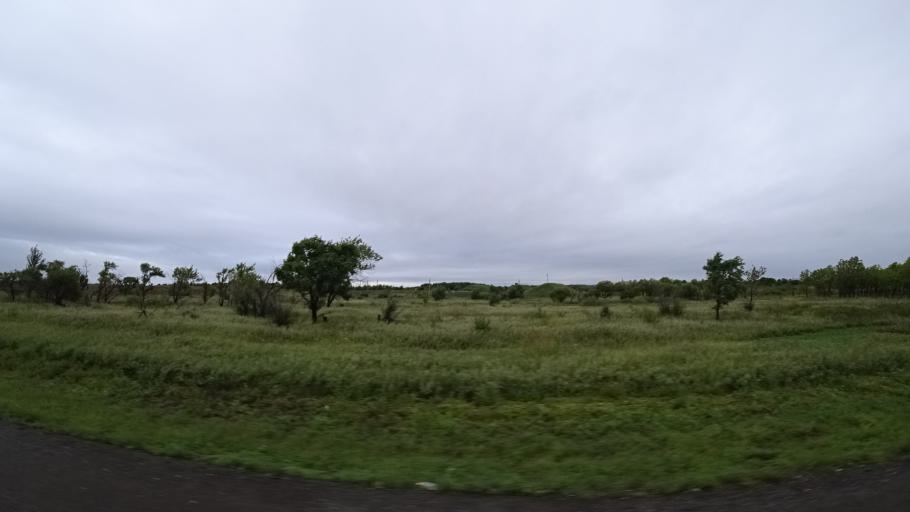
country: RU
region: Primorskiy
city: Chernigovka
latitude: 44.3224
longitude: 132.5692
